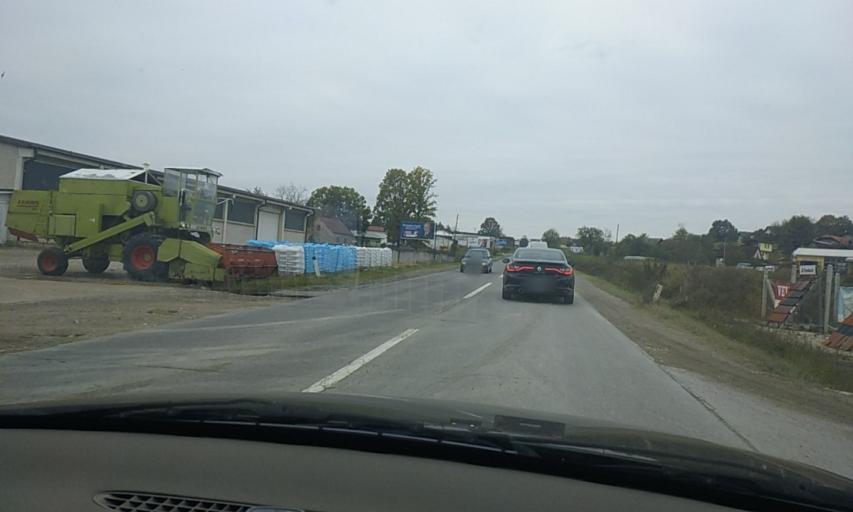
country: BA
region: Republika Srpska
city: Prnjavor
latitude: 44.8571
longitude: 17.6787
